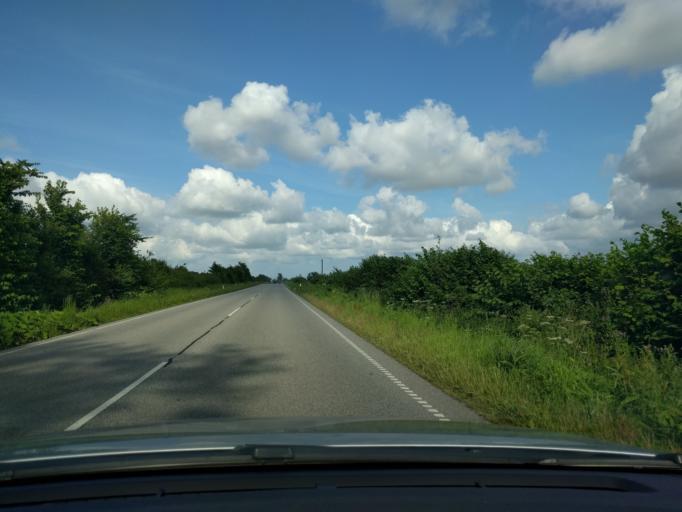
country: DK
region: South Denmark
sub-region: Faaborg-Midtfyn Kommune
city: Ringe
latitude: 55.1744
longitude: 10.5089
